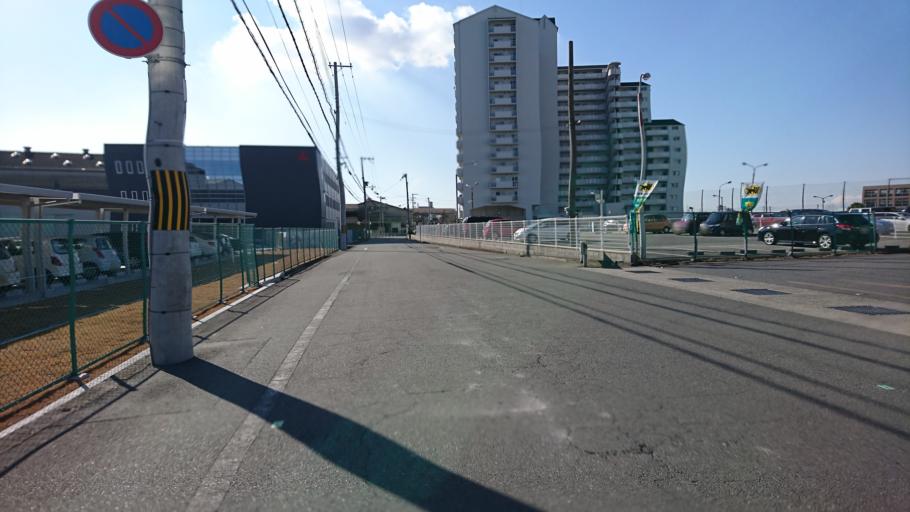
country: JP
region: Hyogo
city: Kakogawacho-honmachi
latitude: 34.7327
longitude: 134.8660
